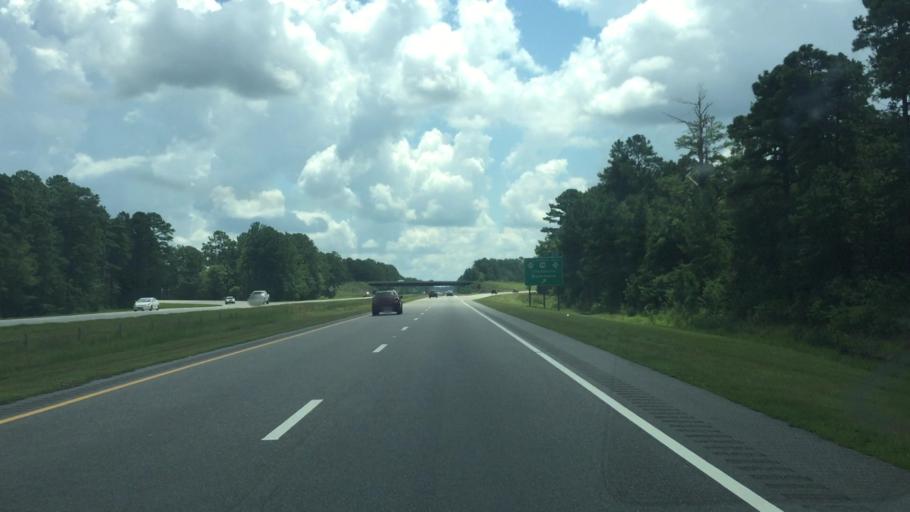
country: US
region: North Carolina
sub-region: Columbus County
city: Chadbourn
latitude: 34.3641
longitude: -78.8345
